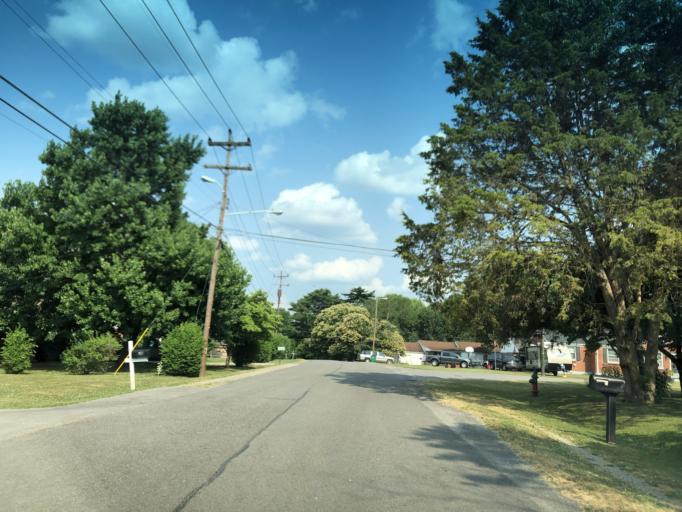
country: US
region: Tennessee
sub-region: Davidson County
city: Goodlettsville
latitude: 36.2558
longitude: -86.7257
